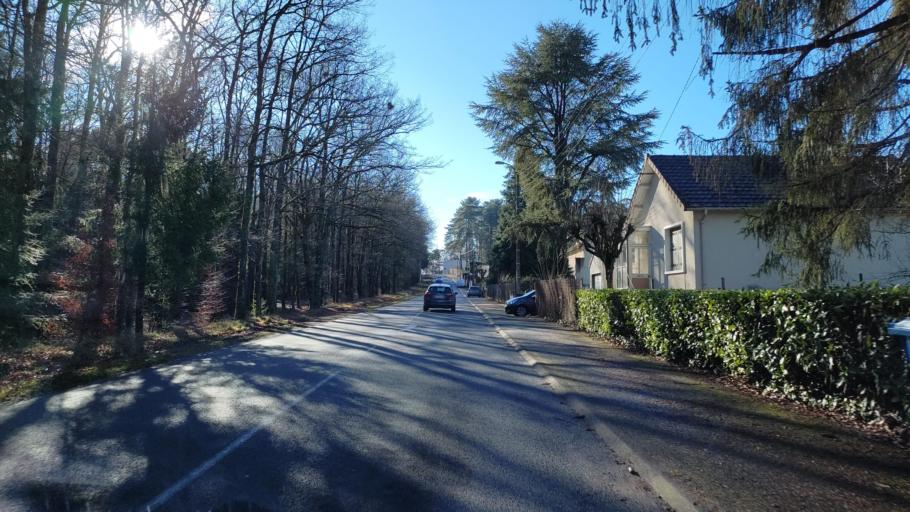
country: FR
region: Limousin
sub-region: Departement de la Haute-Vienne
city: Isle
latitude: 45.8108
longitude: 1.2147
